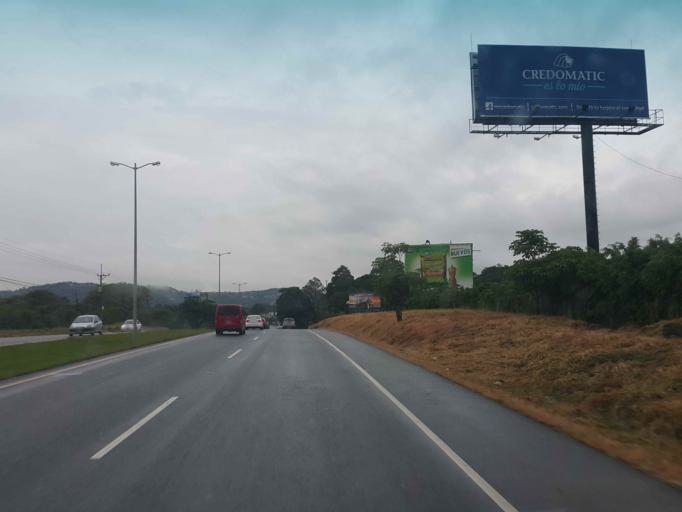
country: CR
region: San Jose
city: Santa Ana
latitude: 9.9376
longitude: -84.2093
